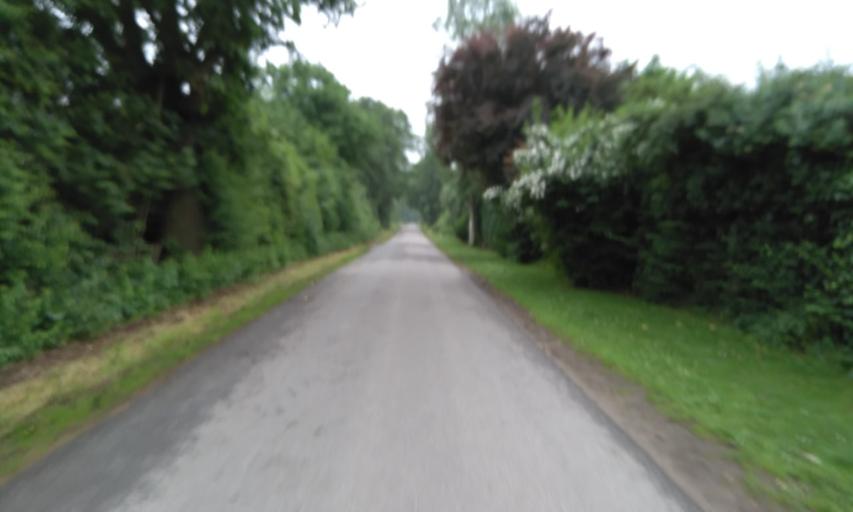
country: DE
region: Lower Saxony
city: Horneburg
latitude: 53.5147
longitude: 9.5760
